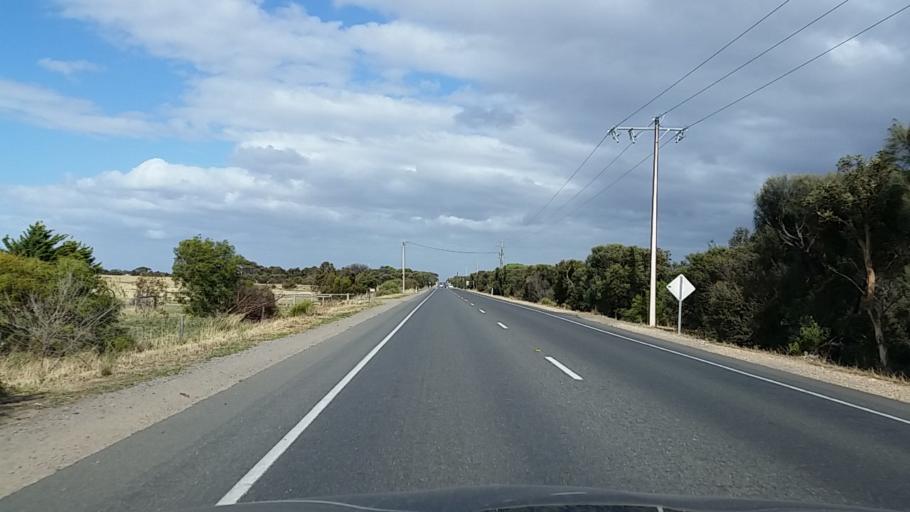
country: AU
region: South Australia
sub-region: Alexandrina
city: Goolwa
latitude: -35.5065
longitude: 138.7564
